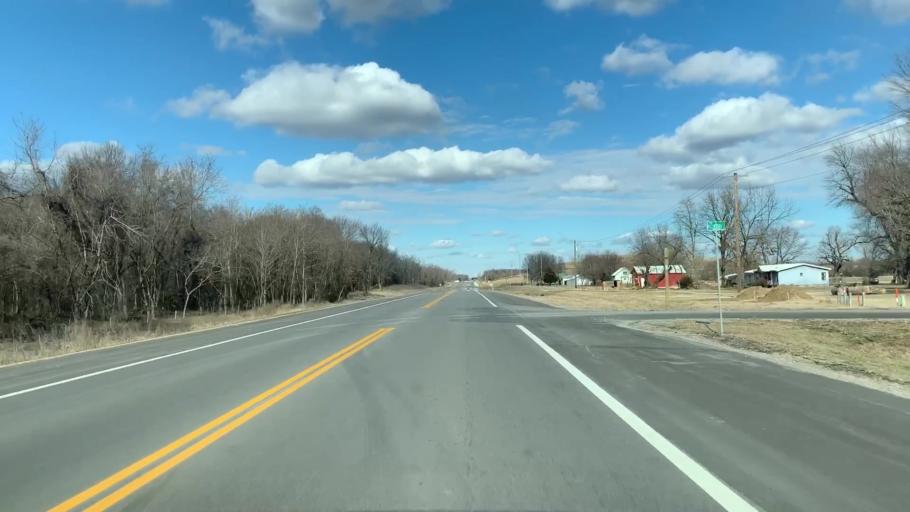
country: US
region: Kansas
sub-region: Cherokee County
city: Columbus
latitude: 37.2318
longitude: -94.8319
